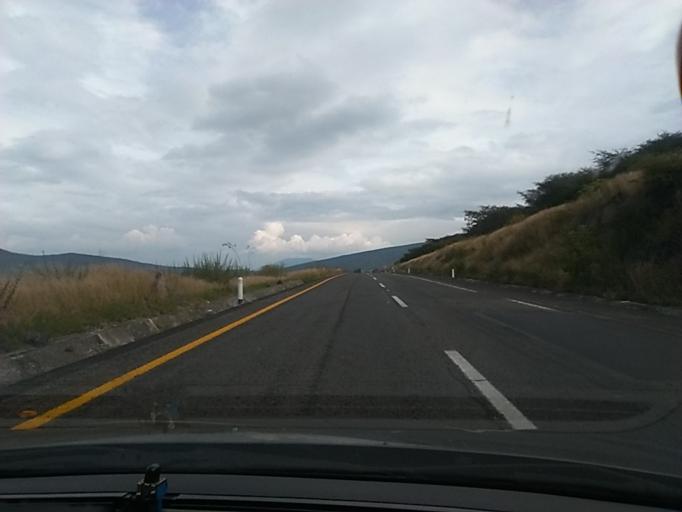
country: MX
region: Michoacan
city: Ixtlan
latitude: 20.2339
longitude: -102.3809
